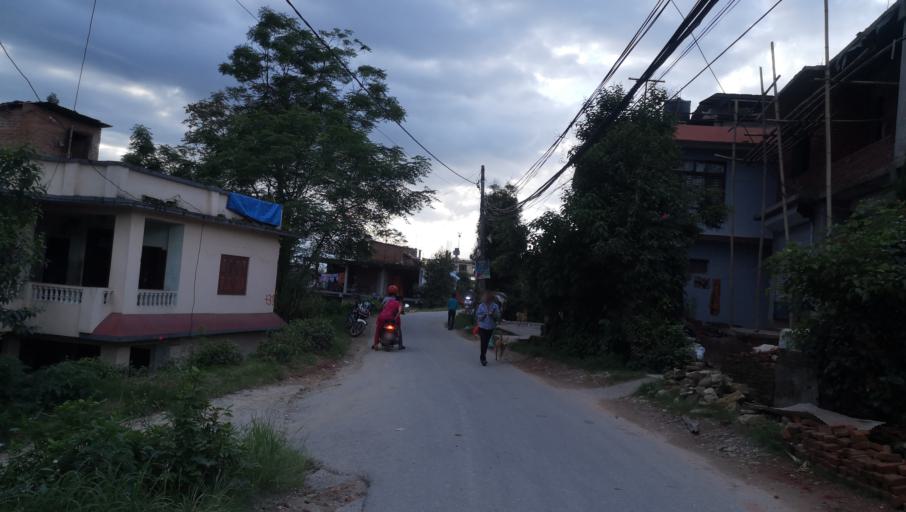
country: NP
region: Central Region
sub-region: Bagmati Zone
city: Bhaktapur
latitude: 27.6493
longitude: 85.3854
